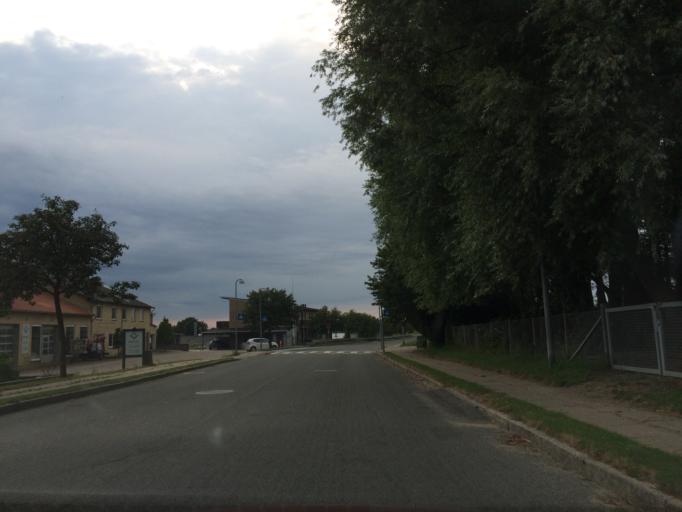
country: DK
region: South Denmark
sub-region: Sonderborg Kommune
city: Broager
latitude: 54.8869
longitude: 9.6712
